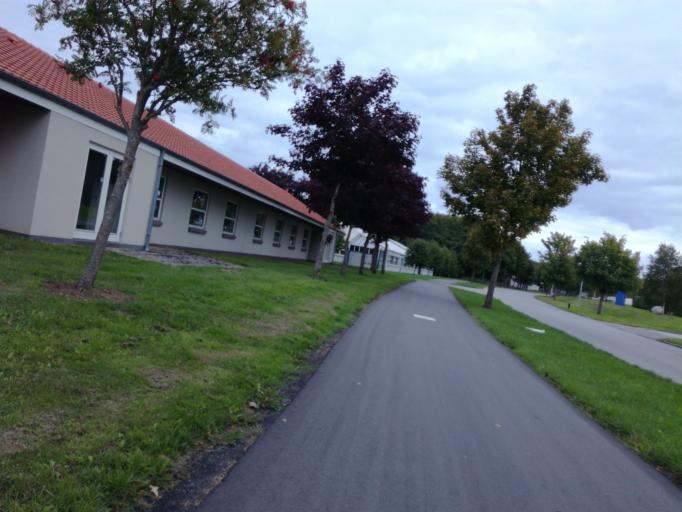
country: DK
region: South Denmark
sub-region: Vejle Kommune
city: Vejle
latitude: 55.6804
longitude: 9.5795
